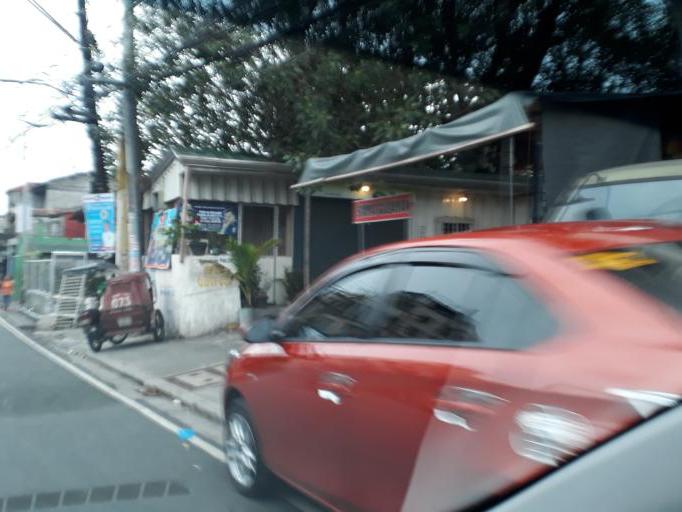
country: PH
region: Calabarzon
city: Del Monte
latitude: 14.6426
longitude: 121.0262
